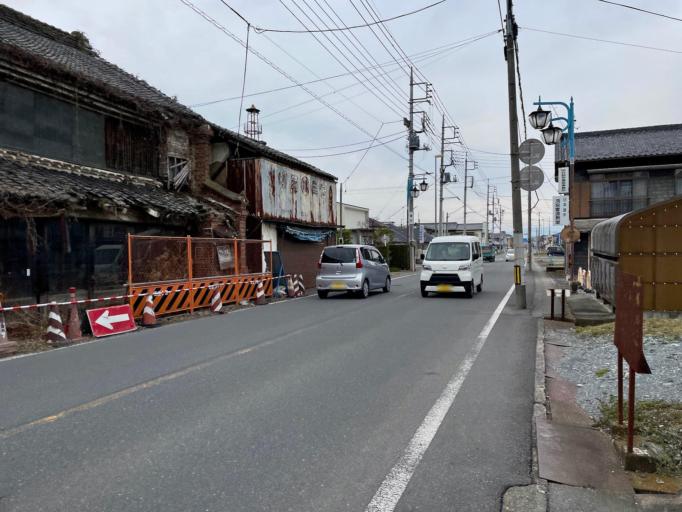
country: JP
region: Saitama
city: Kodamacho-kodamaminami
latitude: 36.1934
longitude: 139.1316
